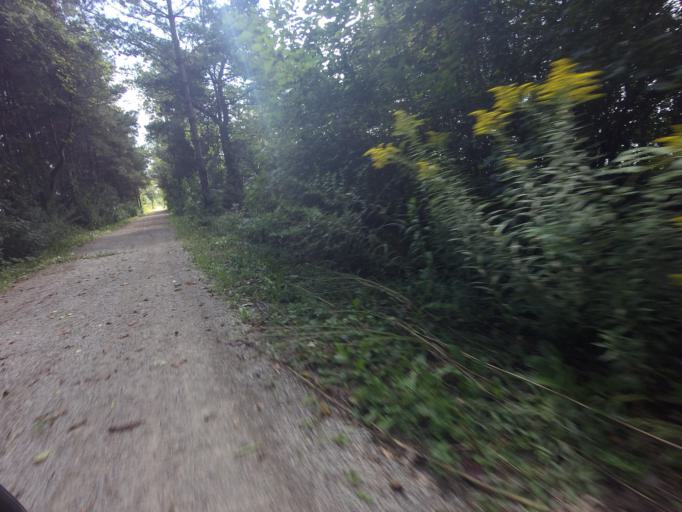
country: CA
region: Ontario
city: Huron East
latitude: 43.6994
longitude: -81.3461
